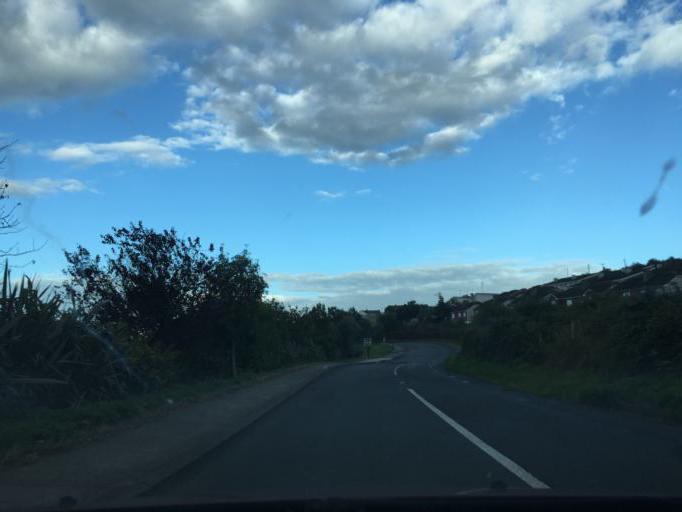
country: IE
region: Leinster
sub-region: Wicklow
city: Wicklow
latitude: 52.9722
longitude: -6.0508
